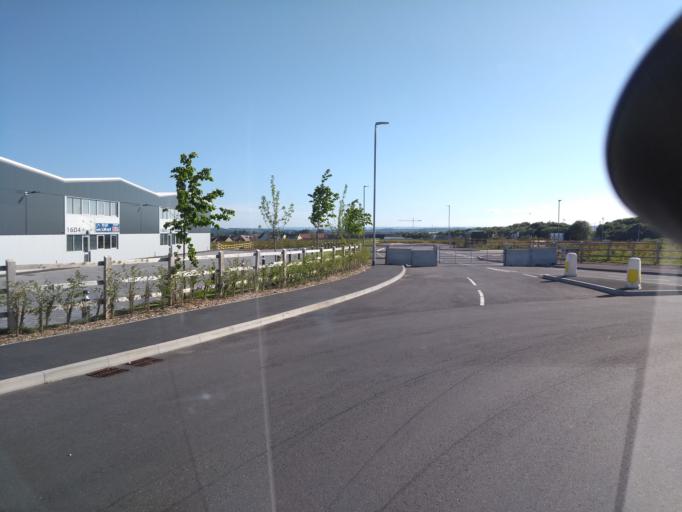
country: GB
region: England
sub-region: Somerset
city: North Petherton
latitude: 51.1025
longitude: -3.0025
